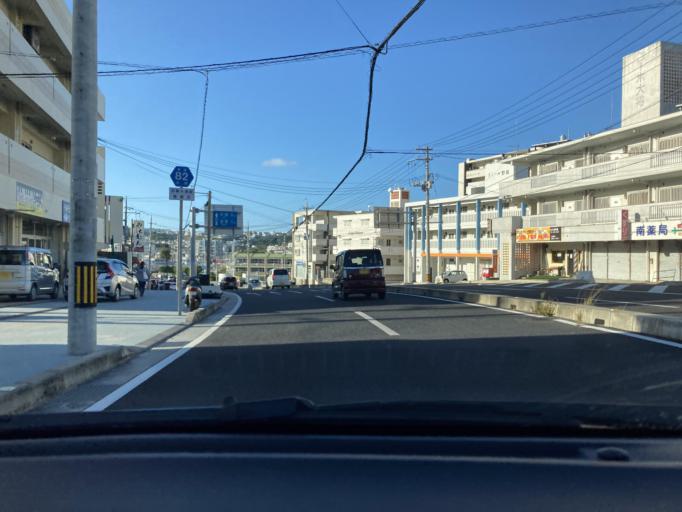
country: JP
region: Okinawa
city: Tomigusuku
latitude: 26.1898
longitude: 127.7304
